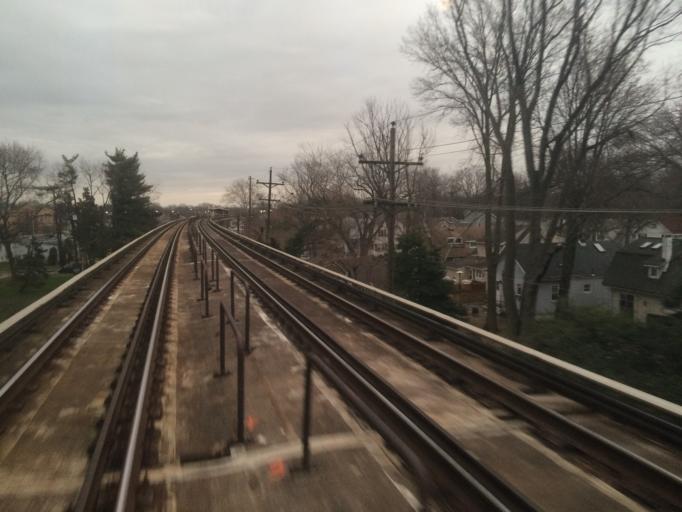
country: US
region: New Jersey
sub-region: Camden County
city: Haddonfield
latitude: 39.9088
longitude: -75.0500
